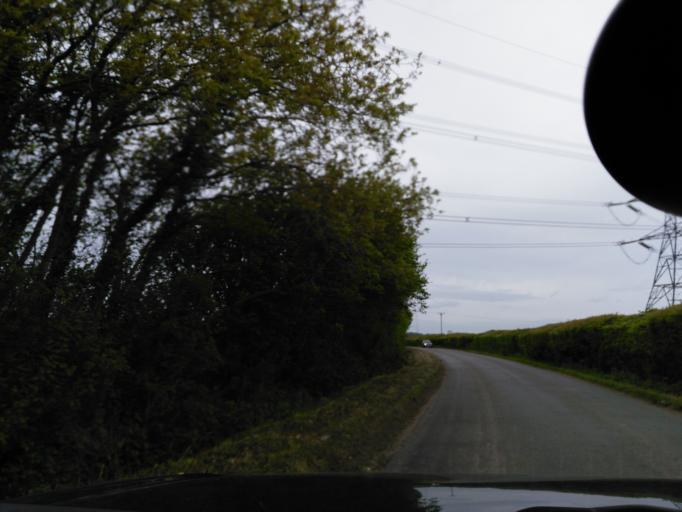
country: GB
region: England
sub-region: Wiltshire
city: Lacock
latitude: 51.4246
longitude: -2.1428
